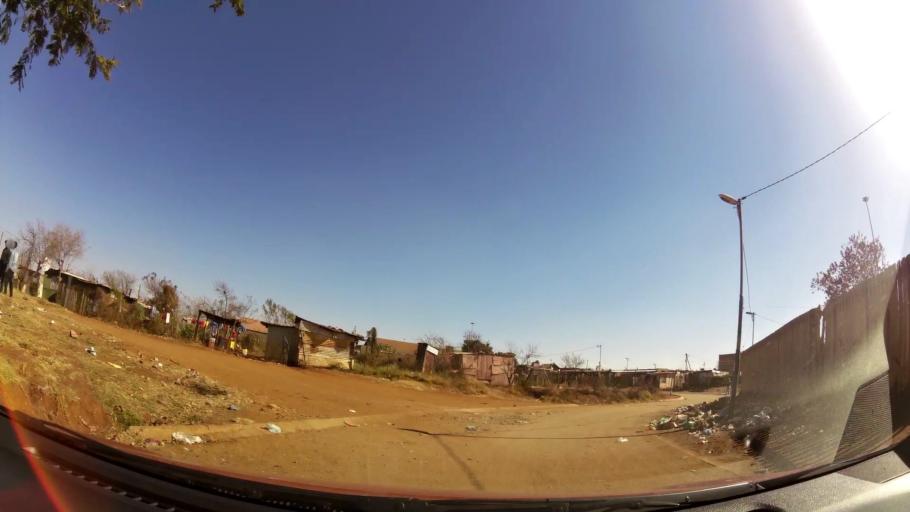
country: ZA
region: Gauteng
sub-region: City of Johannesburg Metropolitan Municipality
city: Soweto
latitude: -26.2170
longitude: 27.8260
